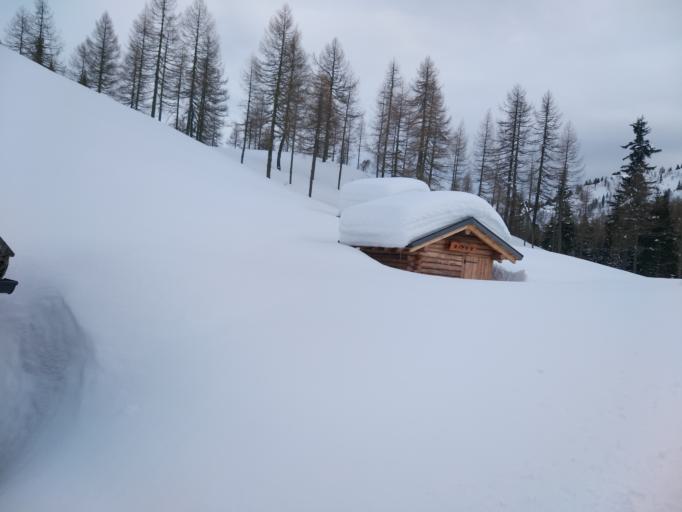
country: IT
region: Veneto
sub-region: Provincia di Belluno
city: Rocca Pietore
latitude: 46.4161
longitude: 11.9771
